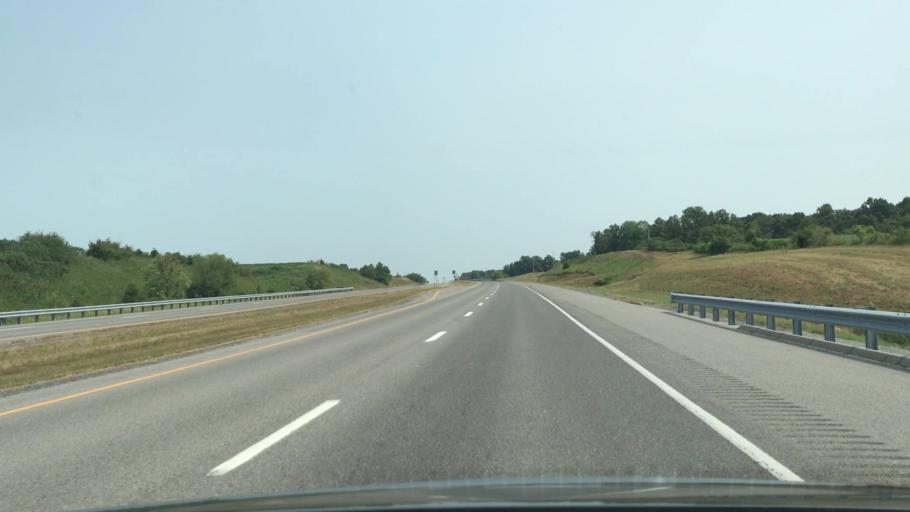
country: US
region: Kentucky
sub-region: Calloway County
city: Murray
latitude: 36.7347
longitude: -88.1698
